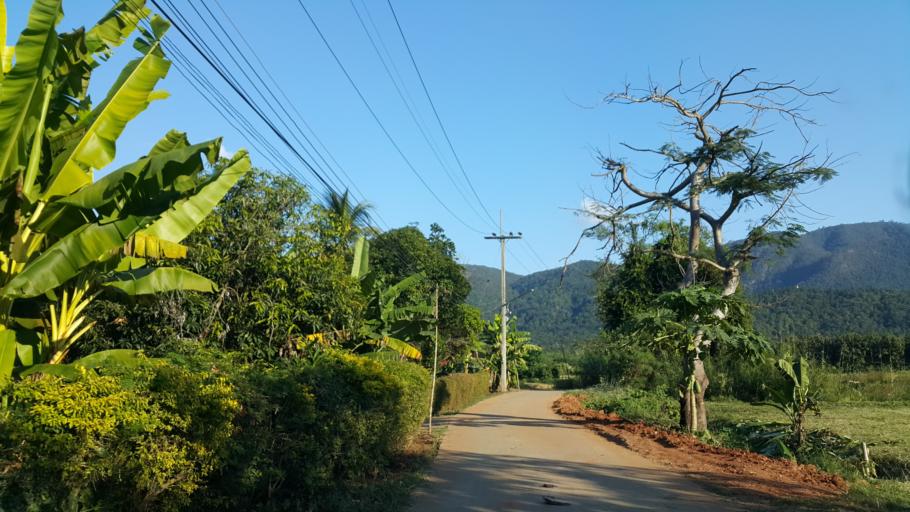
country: TH
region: Chiang Mai
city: Mae On
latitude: 18.7544
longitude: 99.2555
